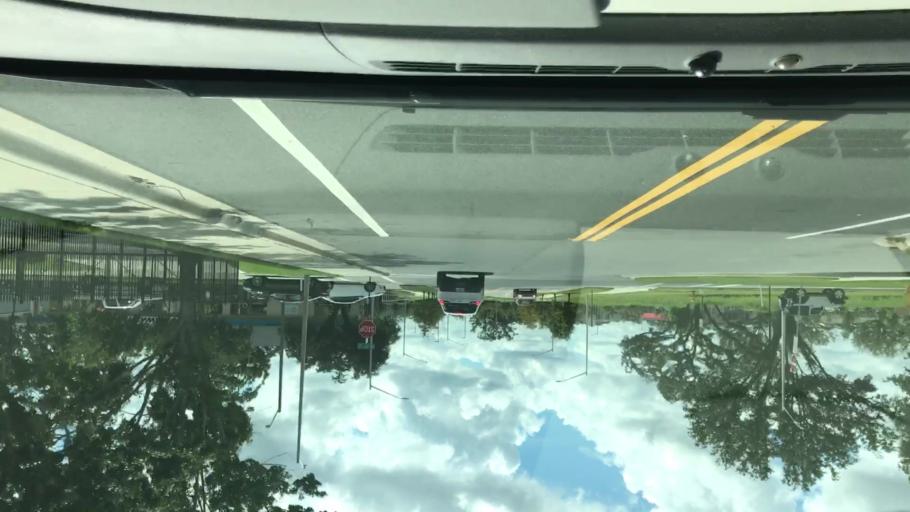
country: US
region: Florida
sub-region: Alachua County
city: Gainesville
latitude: 29.6251
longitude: -82.3874
